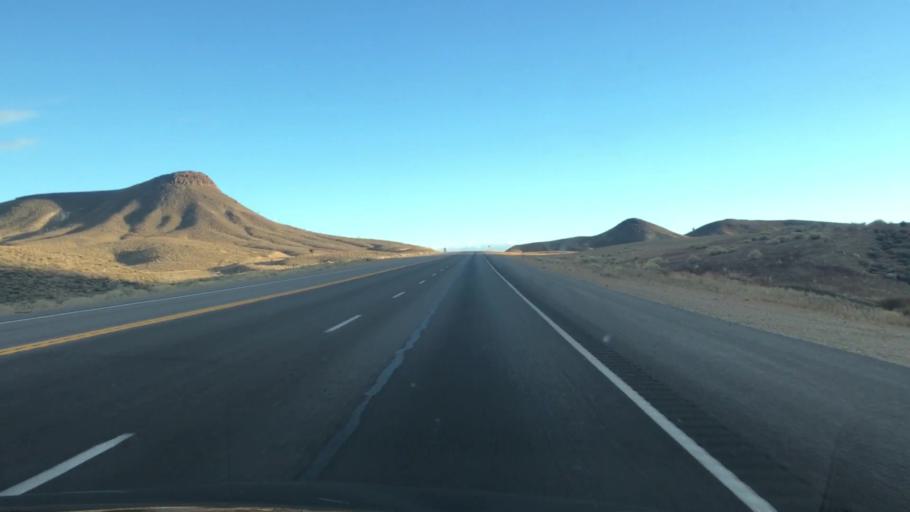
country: US
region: Nevada
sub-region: Esmeralda County
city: Goldfield
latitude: 37.6874
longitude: -117.2329
